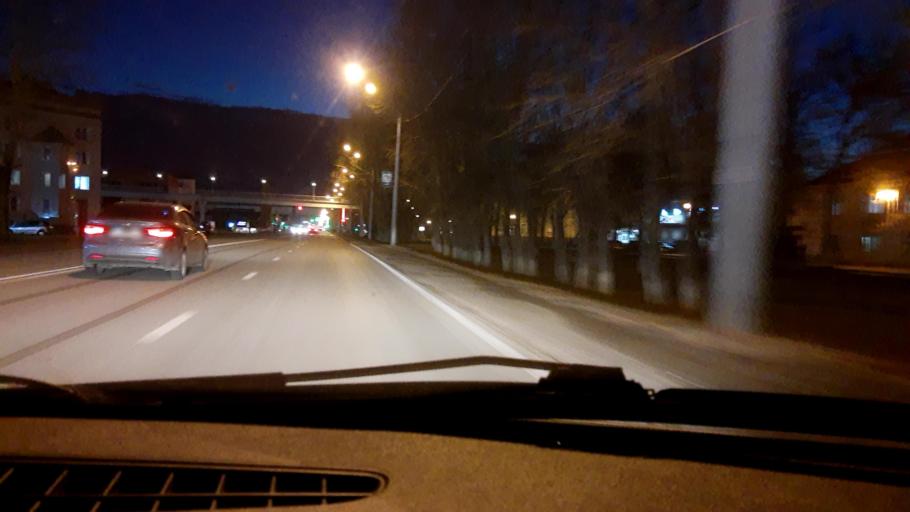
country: RU
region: Bashkortostan
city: Mikhaylovka
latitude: 54.6994
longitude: 55.8375
